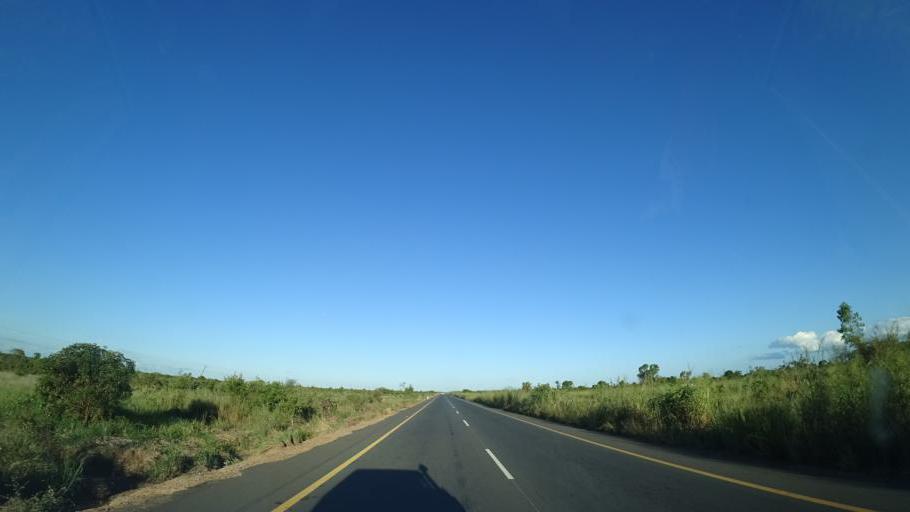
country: MZ
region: Sofala
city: Dondo
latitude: -19.3193
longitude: 34.2908
